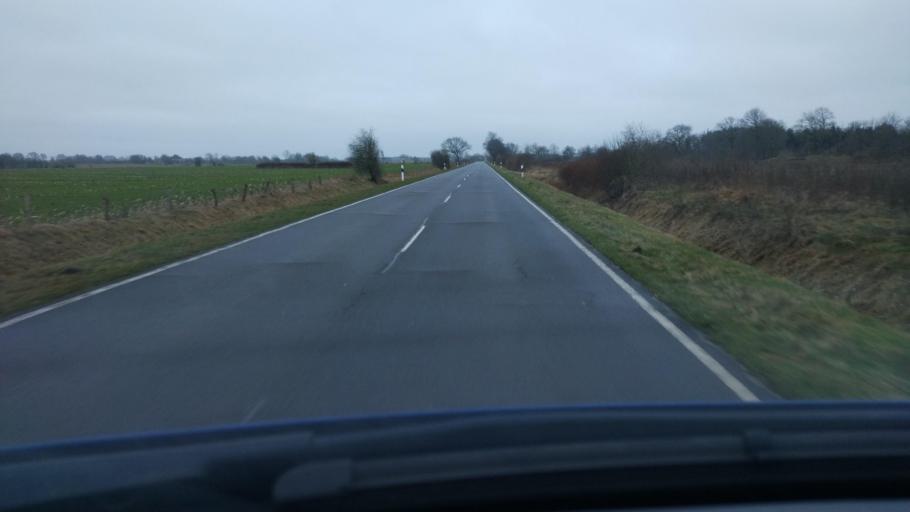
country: DE
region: Schleswig-Holstein
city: Silberstedt
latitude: 54.4990
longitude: 9.3565
